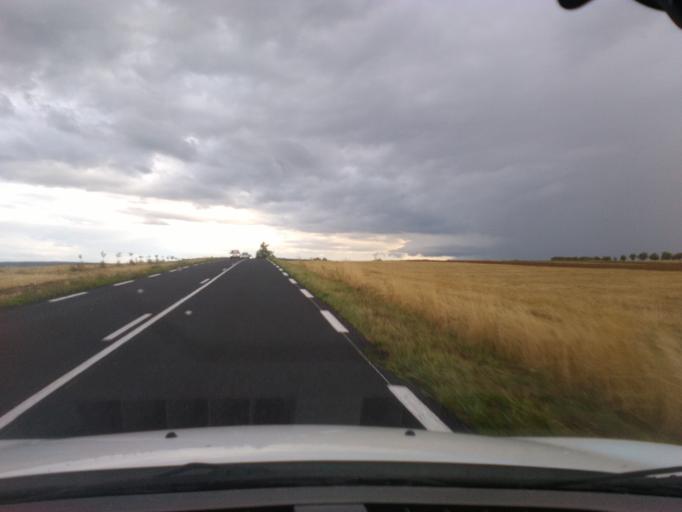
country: FR
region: Lorraine
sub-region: Departement de Meurthe-et-Moselle
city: Vezelise
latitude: 48.4086
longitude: 6.1358
